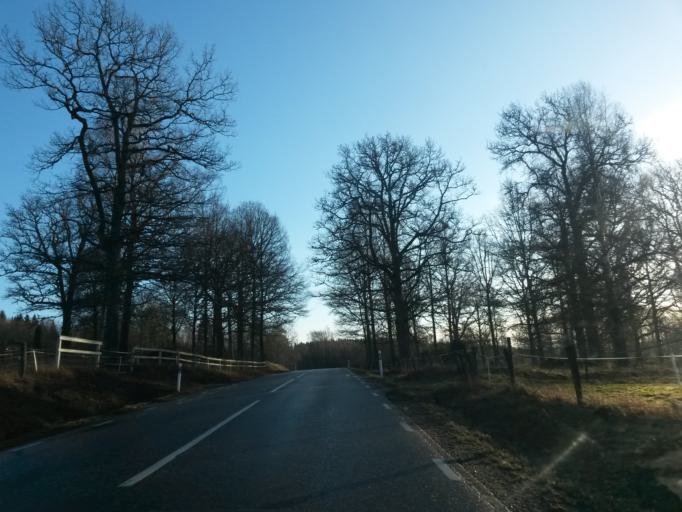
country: SE
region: Vaestra Goetaland
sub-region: Vargarda Kommun
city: Vargarda
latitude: 57.9235
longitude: 12.8649
